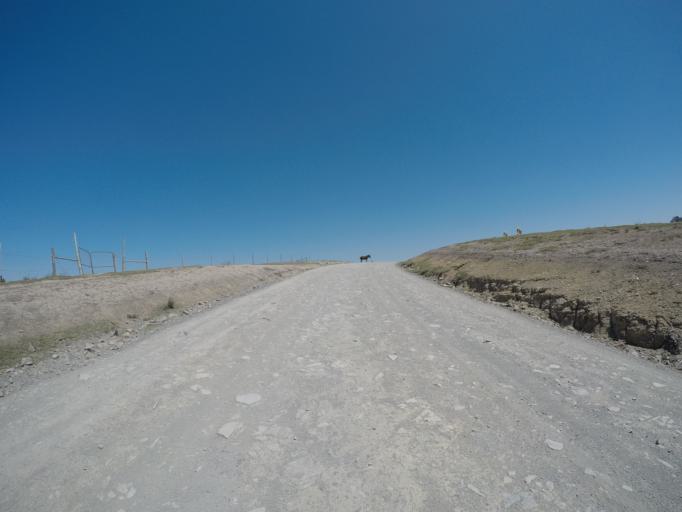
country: ZA
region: Eastern Cape
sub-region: OR Tambo District Municipality
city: Libode
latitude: -31.9945
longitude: 29.0559
